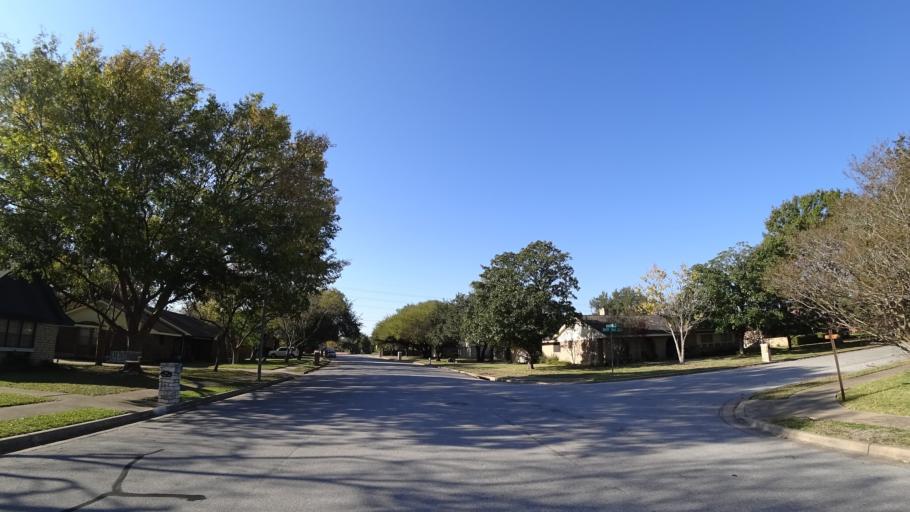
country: US
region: Texas
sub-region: Travis County
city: Shady Hollow
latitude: 30.2198
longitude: -97.8537
